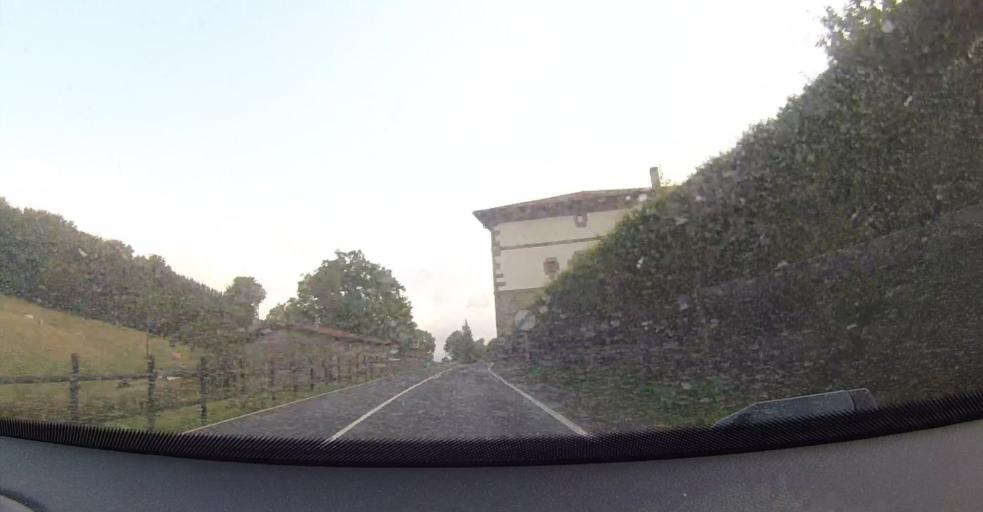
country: ES
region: Basque Country
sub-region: Bizkaia
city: Urrestieta
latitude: 43.2344
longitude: -3.1584
